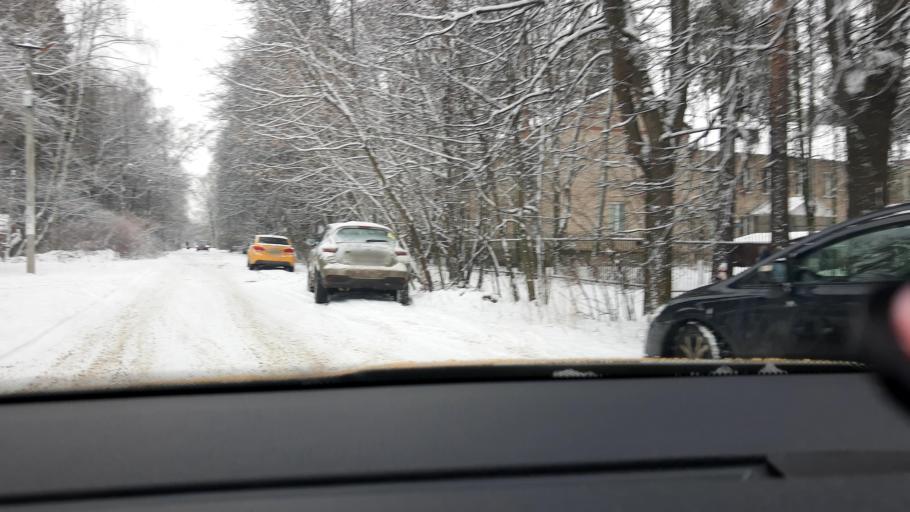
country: RU
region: Moskovskaya
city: Mamontovka
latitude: 55.9829
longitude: 37.8364
